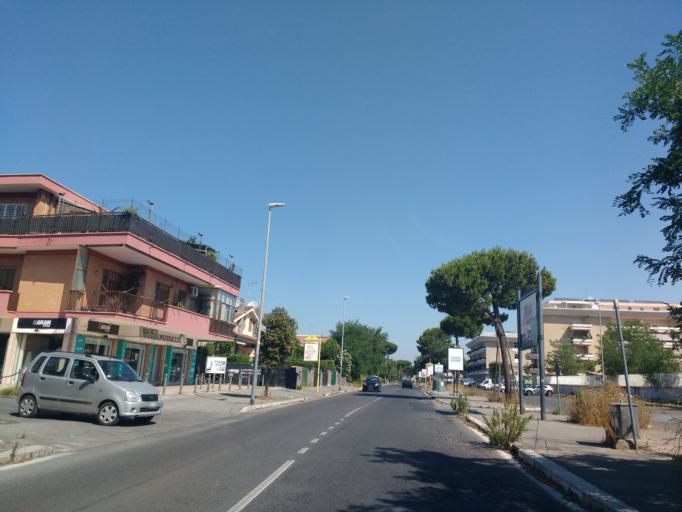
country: IT
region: Latium
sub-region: Citta metropolitana di Roma Capitale
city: Vitinia
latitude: 41.7743
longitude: 12.3707
